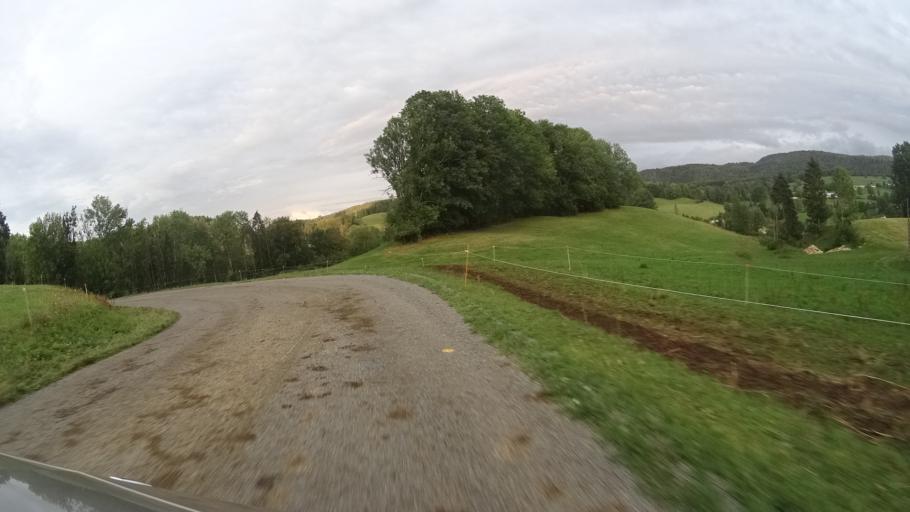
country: FR
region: Franche-Comte
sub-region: Departement du Jura
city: Morbier
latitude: 46.6386
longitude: 6.0249
